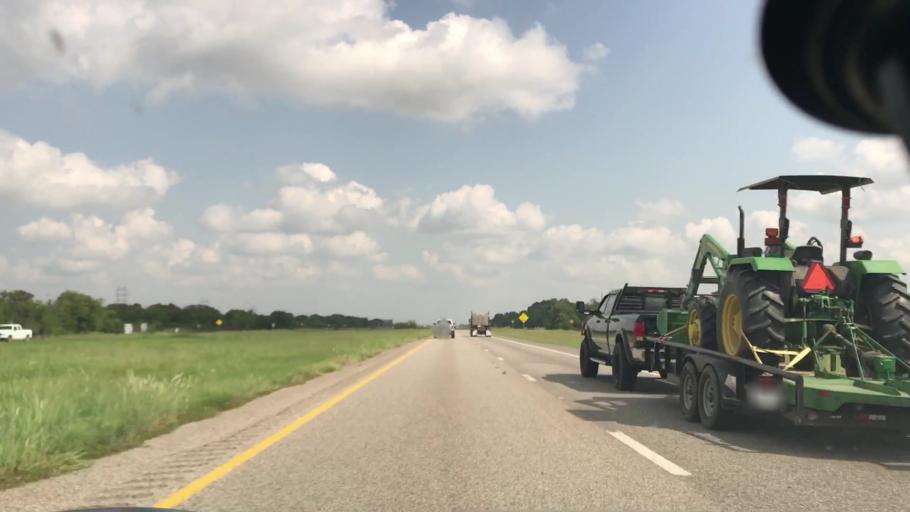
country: US
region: Texas
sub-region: Brazoria County
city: Rosharon
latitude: 29.3902
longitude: -95.4264
